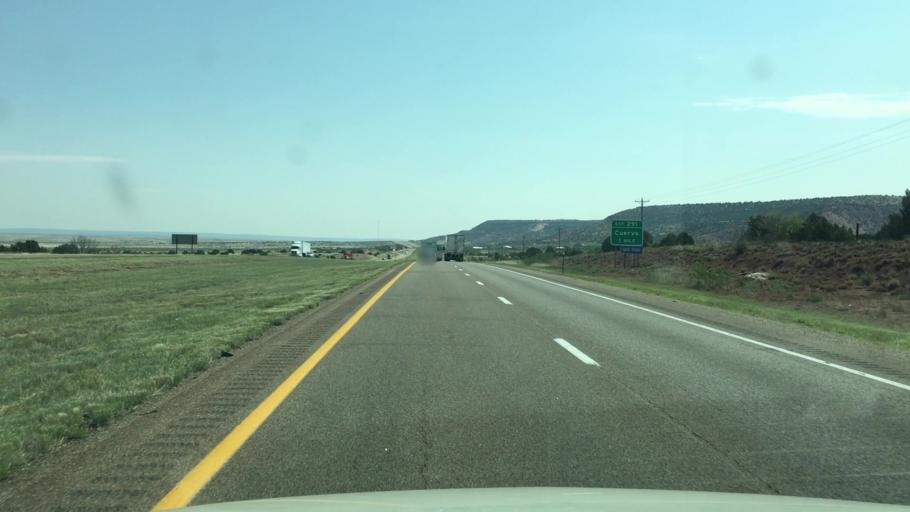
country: US
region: New Mexico
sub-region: Guadalupe County
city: Santa Rosa
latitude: 35.0235
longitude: -104.4269
